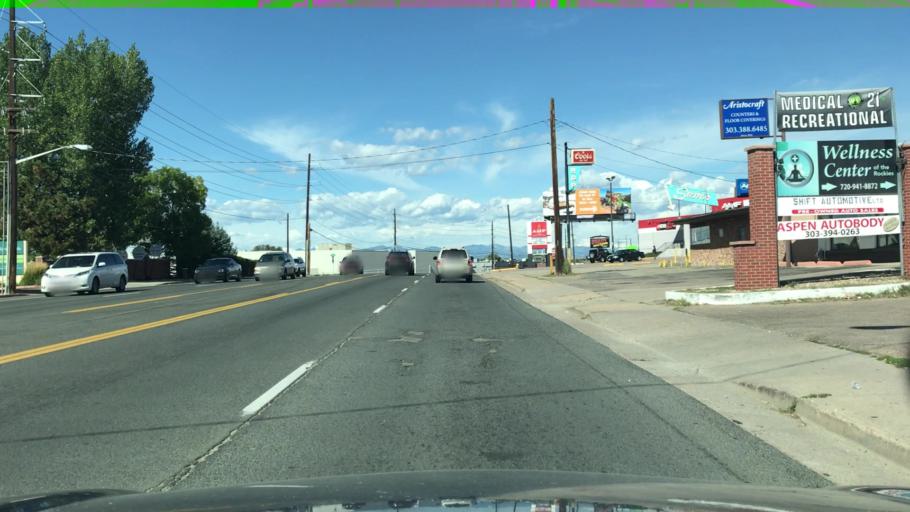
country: US
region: Colorado
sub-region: Arapahoe County
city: Glendale
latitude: 39.7005
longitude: -104.9088
